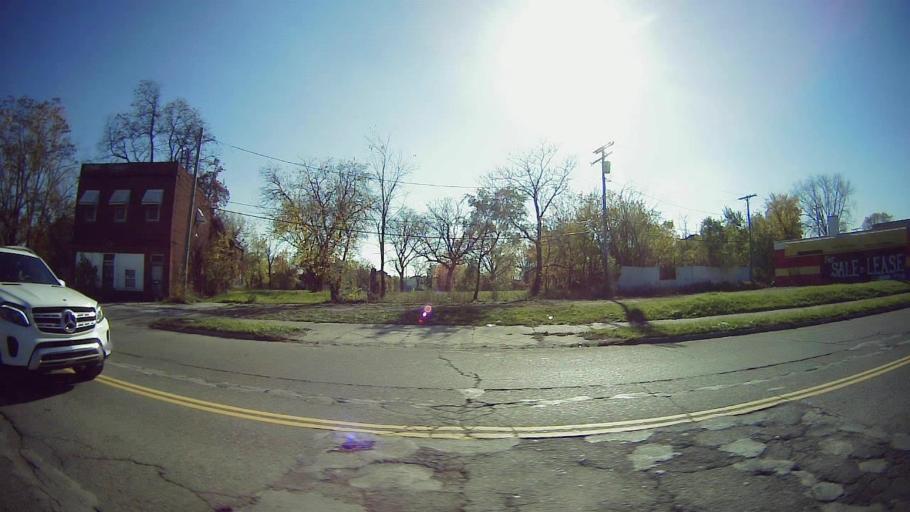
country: US
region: Michigan
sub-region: Wayne County
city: Highland Park
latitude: 42.4180
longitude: -83.0961
